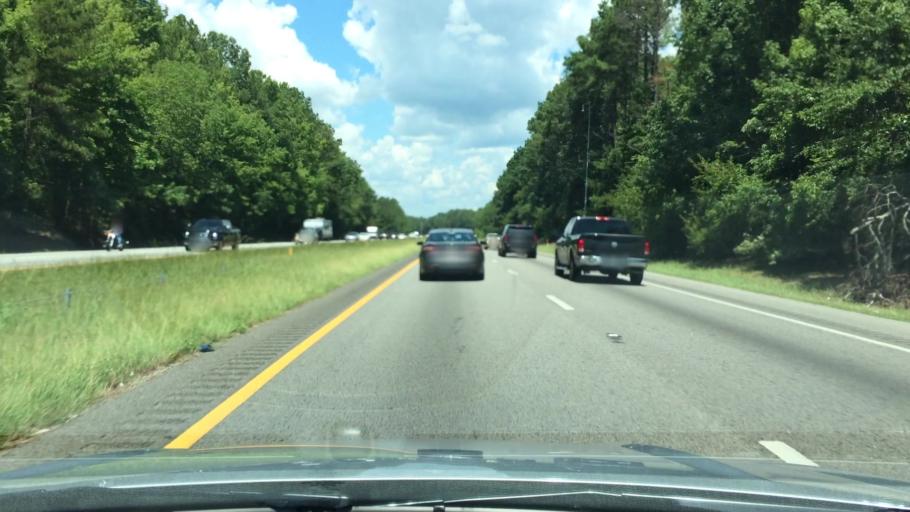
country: US
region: South Carolina
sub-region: Lexington County
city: Irmo
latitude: 34.1281
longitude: -81.2048
